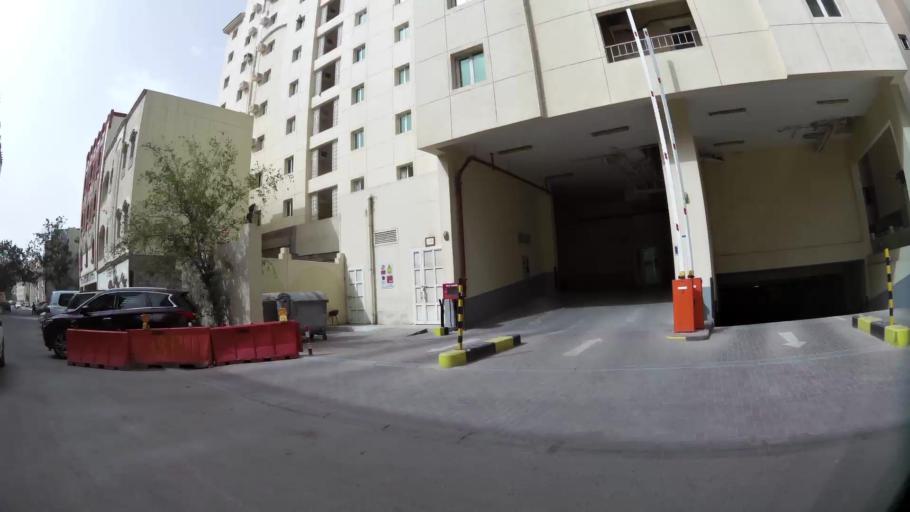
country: QA
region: Baladiyat ad Dawhah
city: Doha
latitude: 25.2742
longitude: 51.5339
